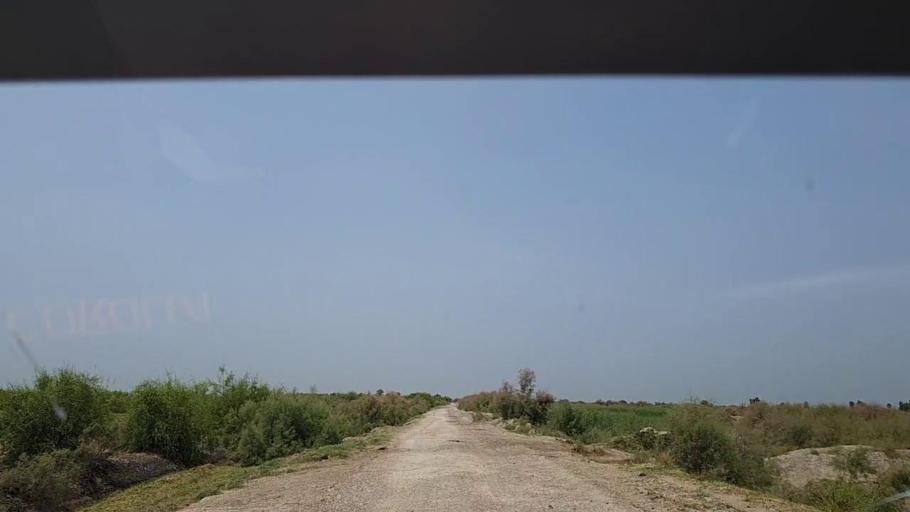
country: PK
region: Sindh
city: Adilpur
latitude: 27.8891
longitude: 69.2536
